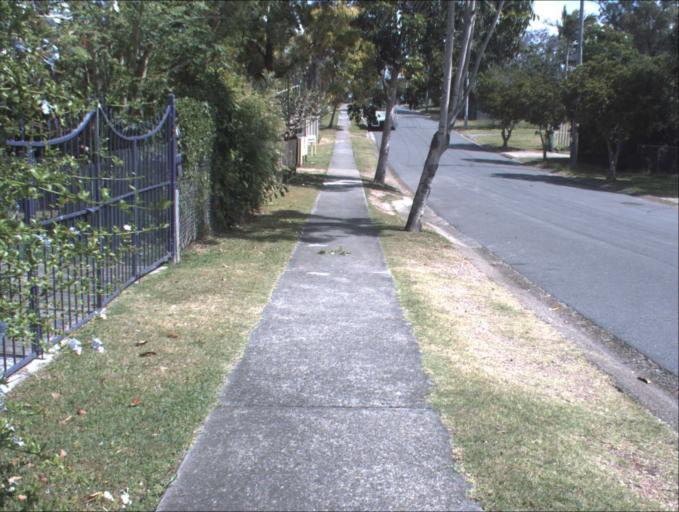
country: AU
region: Queensland
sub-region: Logan
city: Woodridge
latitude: -27.6304
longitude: 153.1013
